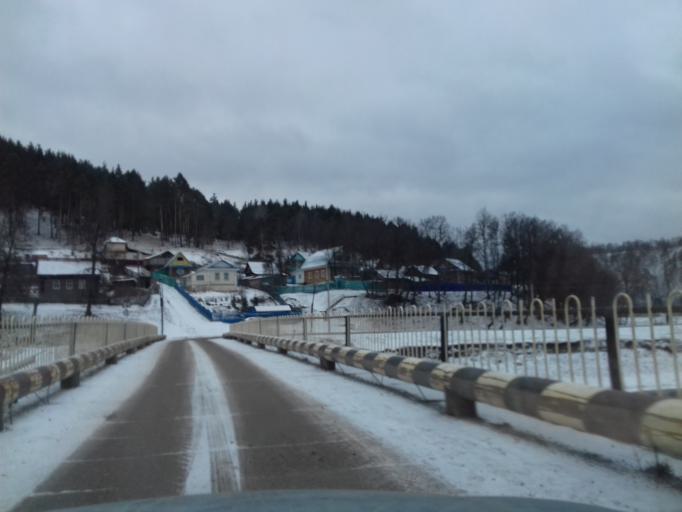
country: RU
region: Bashkortostan
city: Starosubkhangulovo
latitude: 53.0948
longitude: 57.4290
